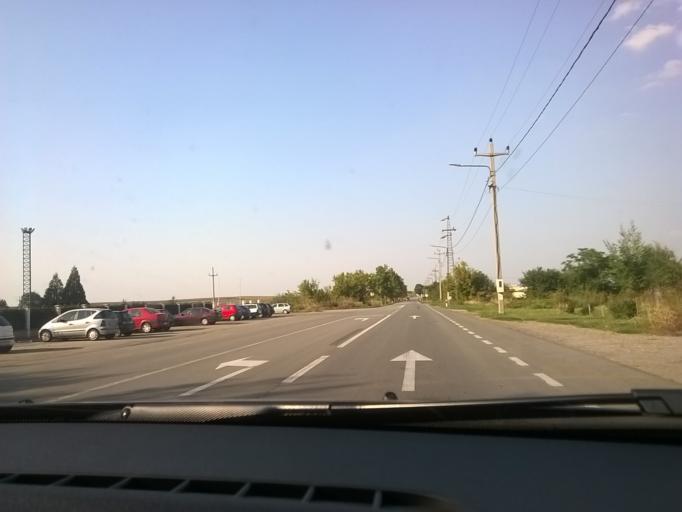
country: RS
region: Autonomna Pokrajina Vojvodina
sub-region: Juznobanatski Okrug
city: Vrsac
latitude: 45.1365
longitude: 21.2872
